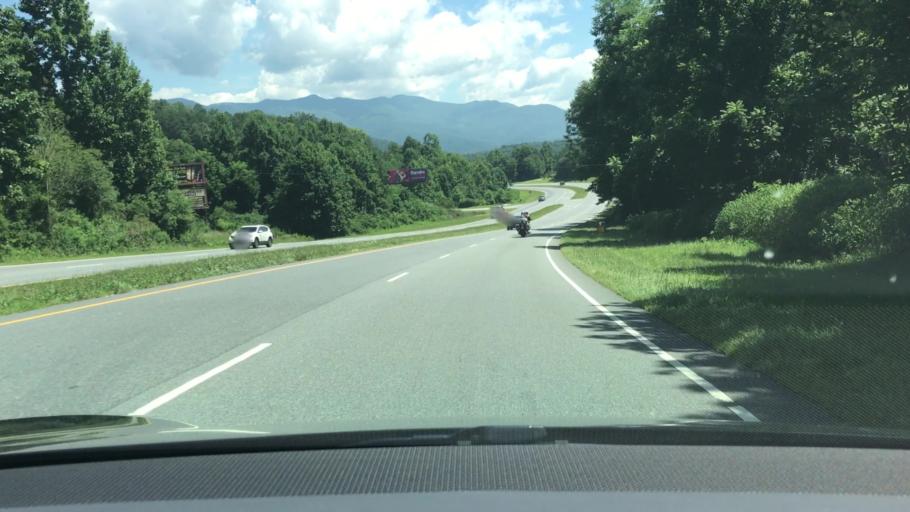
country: US
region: North Carolina
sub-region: Jackson County
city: Sylva
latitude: 35.3562
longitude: -83.2565
